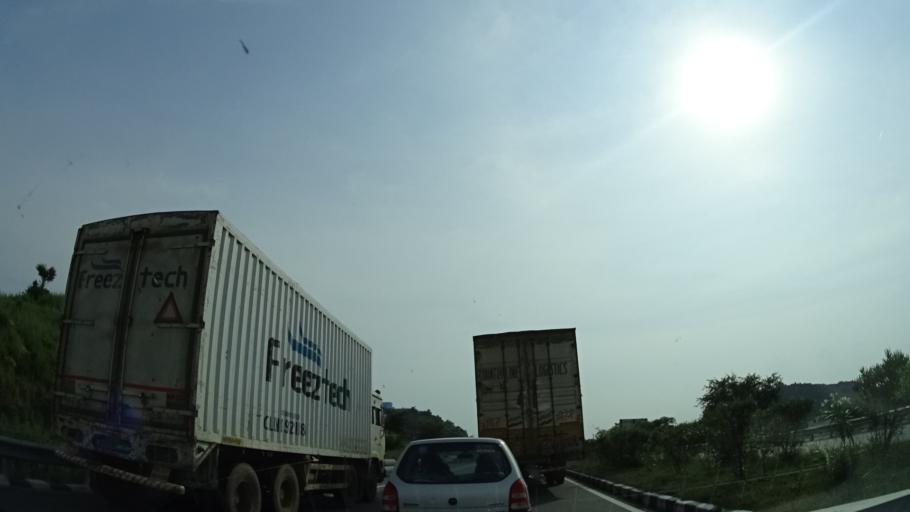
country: IN
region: Telangana
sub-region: Adilabad
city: Nirmal
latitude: 18.8708
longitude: 78.3452
